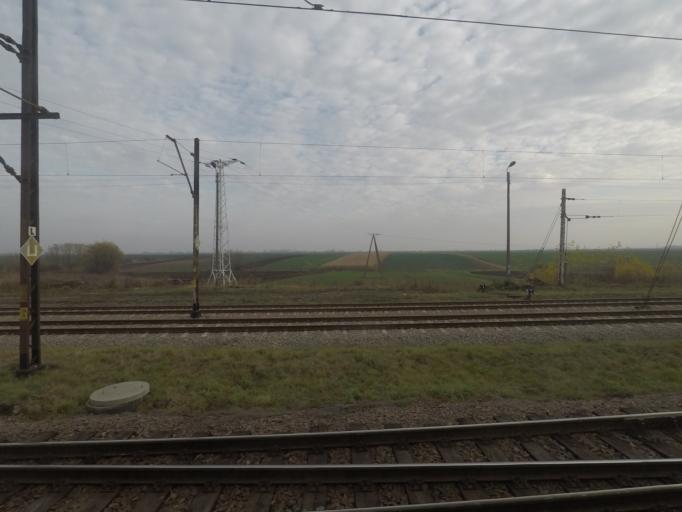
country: PL
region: Subcarpathian Voivodeship
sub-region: Powiat przemyski
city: Orly
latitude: 49.8444
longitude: 22.8469
